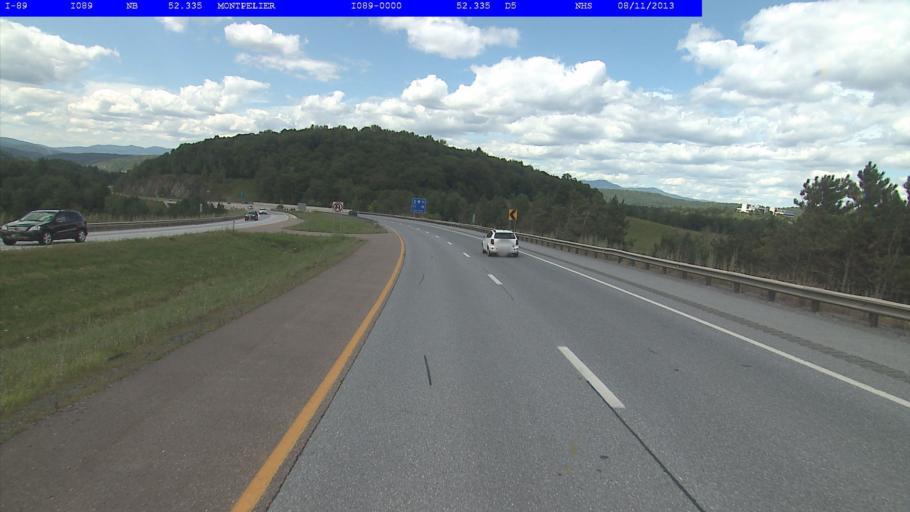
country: US
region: Vermont
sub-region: Washington County
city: Montpelier
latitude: 44.2451
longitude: -72.5865
